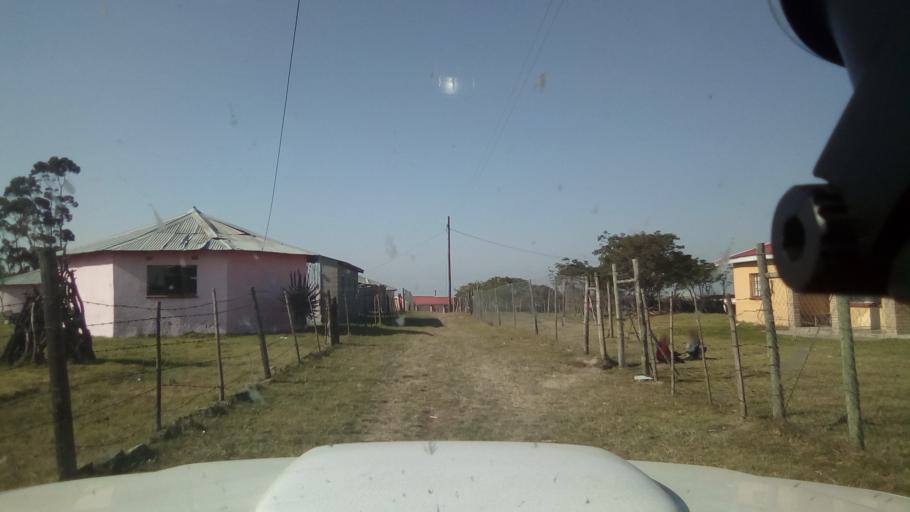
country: ZA
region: Eastern Cape
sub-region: Buffalo City Metropolitan Municipality
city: Bhisho
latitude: -32.9430
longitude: 27.3374
